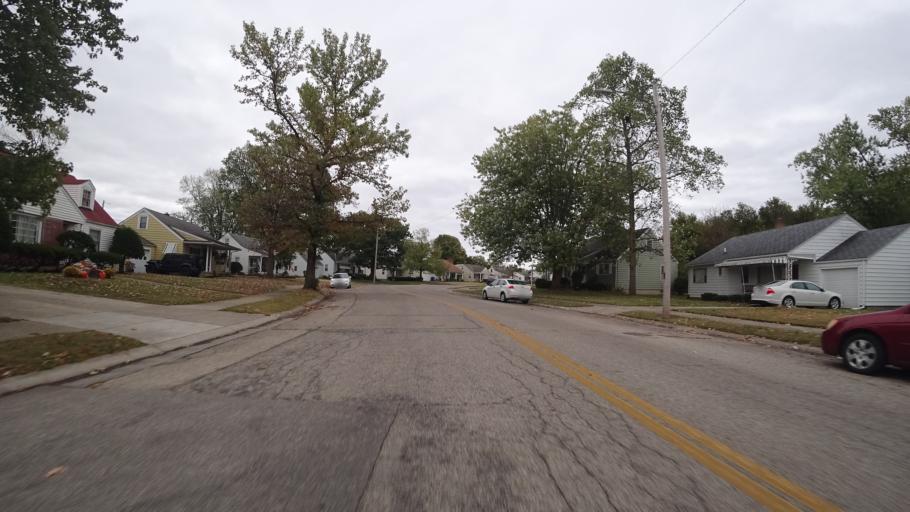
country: US
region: Ohio
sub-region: Butler County
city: Fairfield
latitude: 39.3624
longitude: -84.5607
